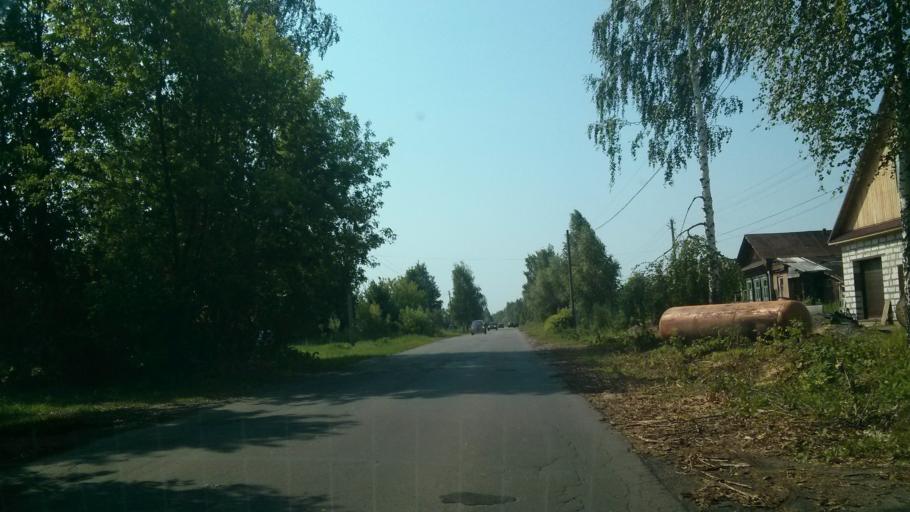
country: RU
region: Vladimir
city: Murom
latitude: 55.5367
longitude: 42.0244
